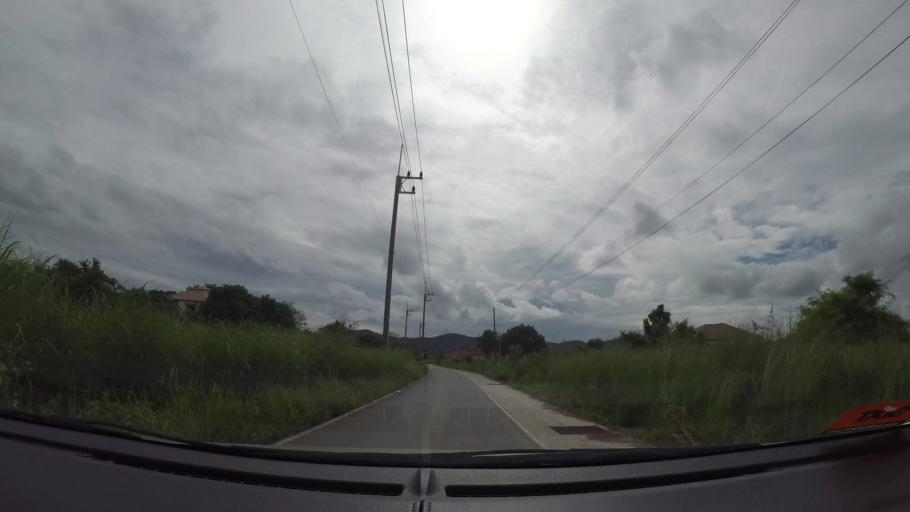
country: TH
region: Chon Buri
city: Sattahip
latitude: 12.7135
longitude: 100.8998
